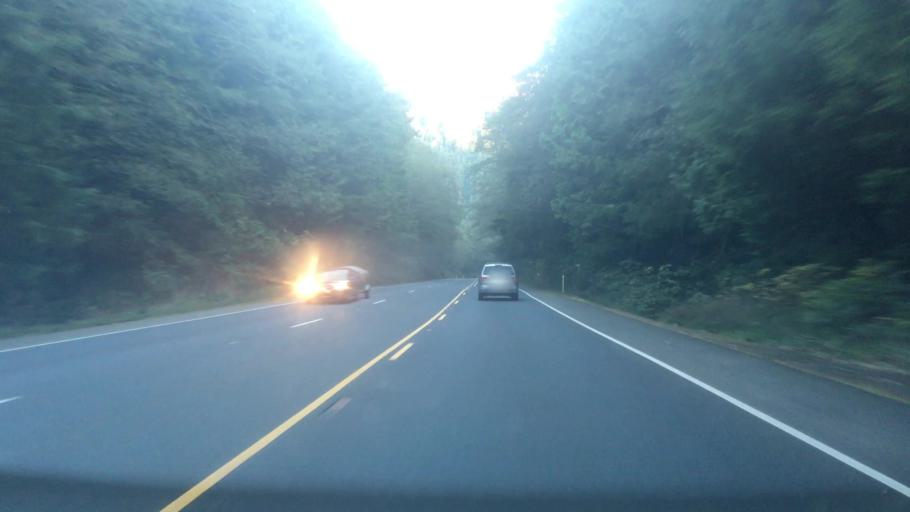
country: US
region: Oregon
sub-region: Clatsop County
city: Cannon Beach
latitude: 45.7778
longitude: -123.9505
